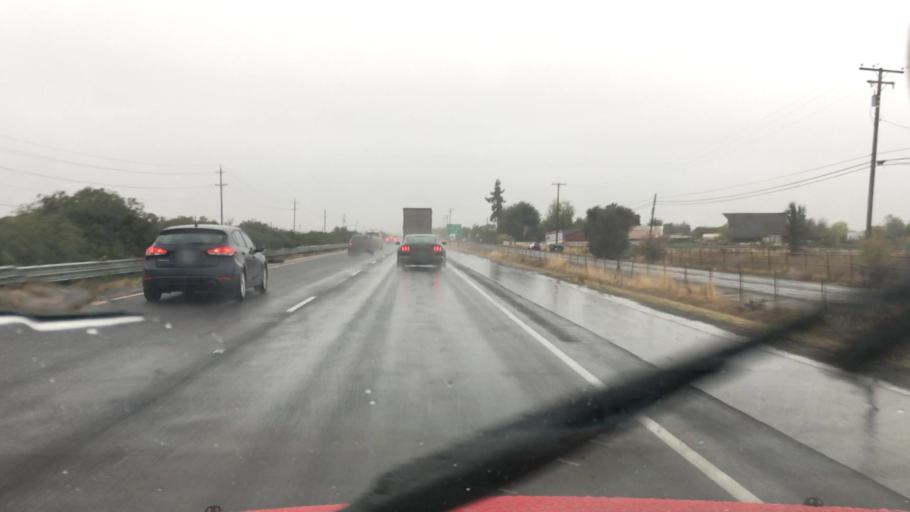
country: US
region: California
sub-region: Sacramento County
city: Galt
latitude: 38.3046
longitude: -121.3187
